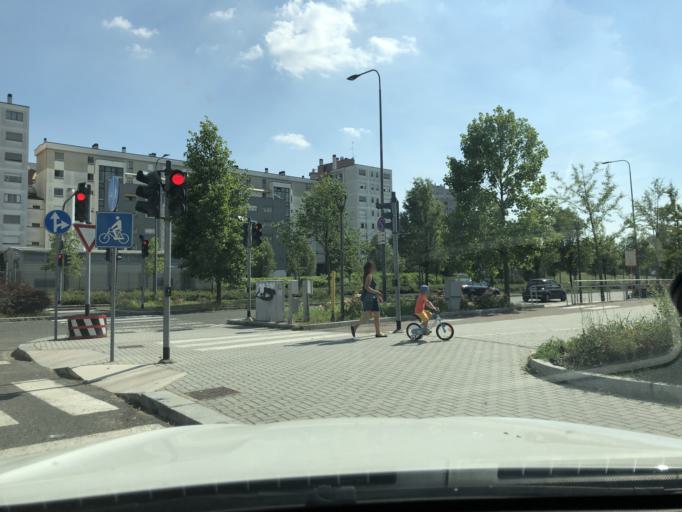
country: IT
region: Lombardy
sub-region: Citta metropolitana di Milano
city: Novate Milanese
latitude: 45.5115
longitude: 9.1412
